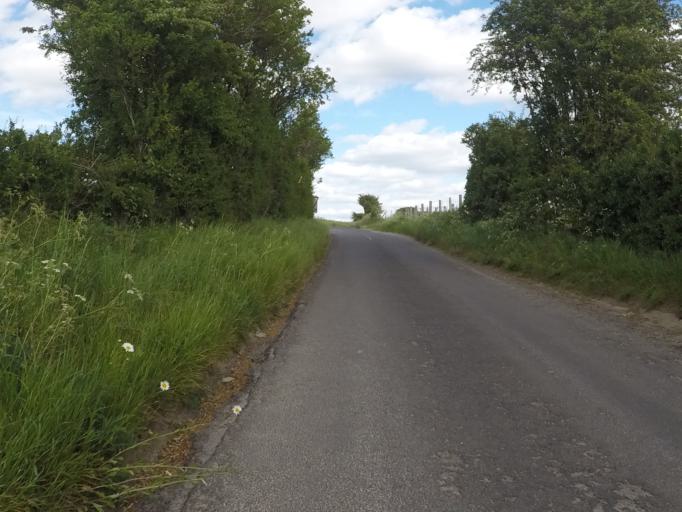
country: GB
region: England
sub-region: Oxfordshire
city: Witney
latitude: 51.8100
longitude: -1.5136
